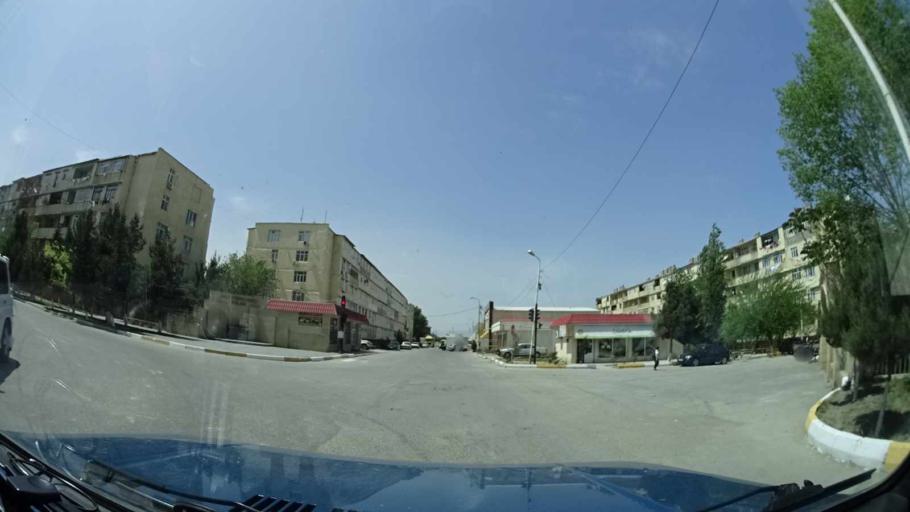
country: AZ
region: Sumqayit
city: Haci Zeynalabdin
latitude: 40.6240
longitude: 49.5664
